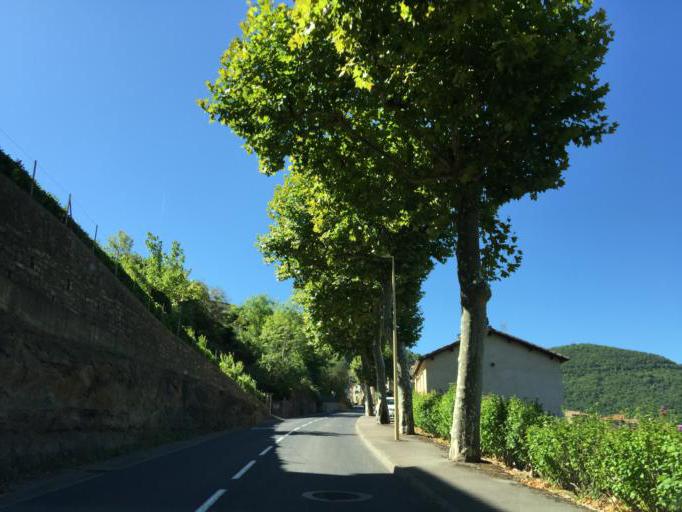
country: FR
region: Midi-Pyrenees
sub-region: Departement de l'Aveyron
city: Saint-Georges-de-Luzencon
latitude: 44.0516
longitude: 2.8994
